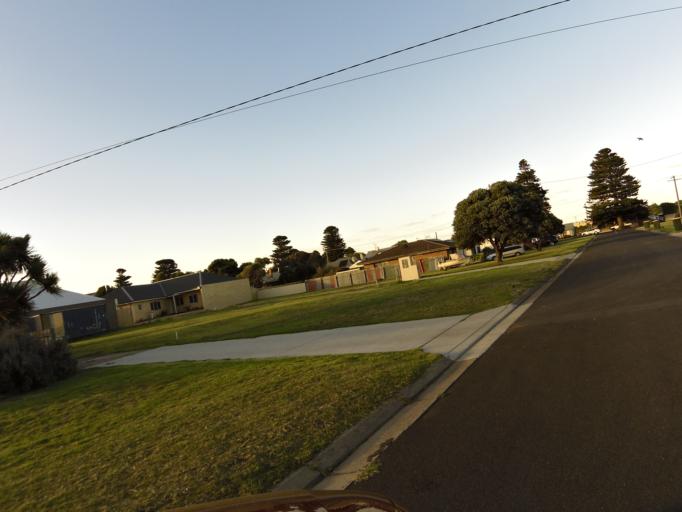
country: AU
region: Victoria
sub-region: Warrnambool
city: Warrnambool
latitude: -38.3957
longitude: 142.4692
